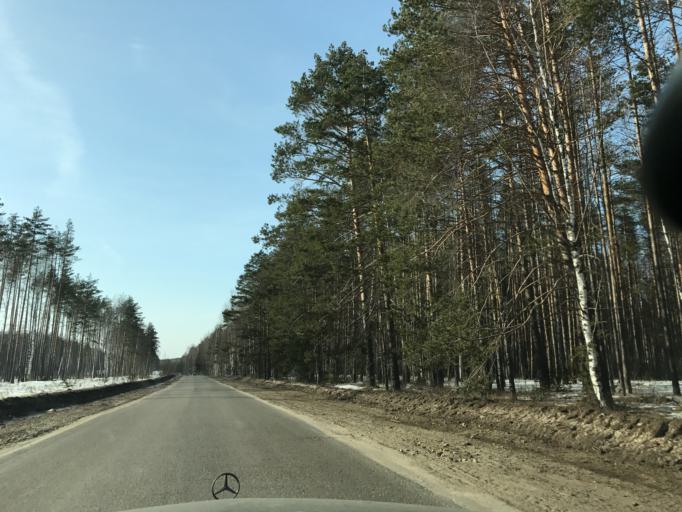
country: RU
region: Nizjnij Novgorod
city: Taremskoye
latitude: 56.0122
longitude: 42.9735
